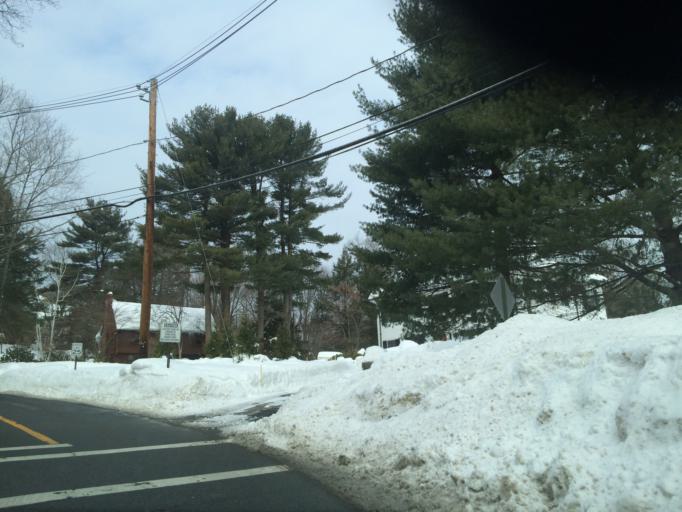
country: US
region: Massachusetts
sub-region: Middlesex County
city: Weston
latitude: 42.3695
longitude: -71.2965
